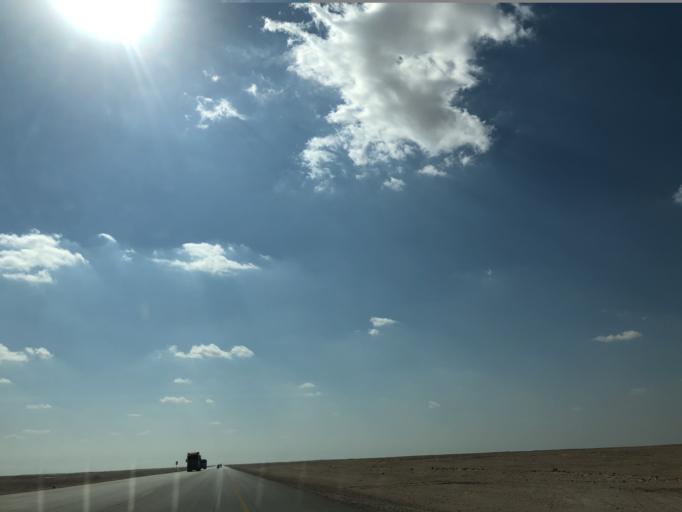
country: OM
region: Al Wusta
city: Hayma'
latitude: 20.1859
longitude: 56.5341
